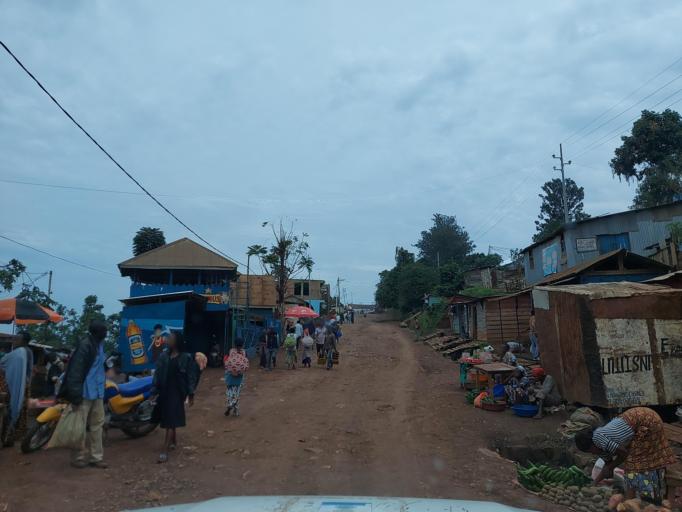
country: CD
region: South Kivu
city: Bukavu
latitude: -2.4702
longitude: 28.8274
